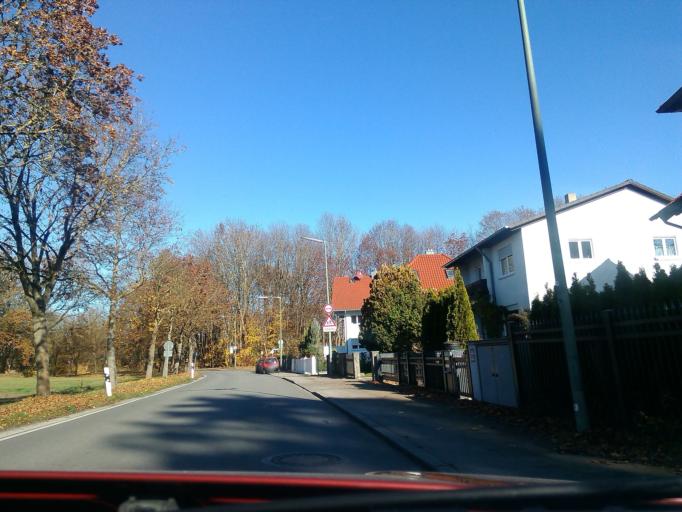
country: DE
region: Bavaria
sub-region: Upper Bavaria
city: Grobenzell
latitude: 48.1747
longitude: 11.4081
